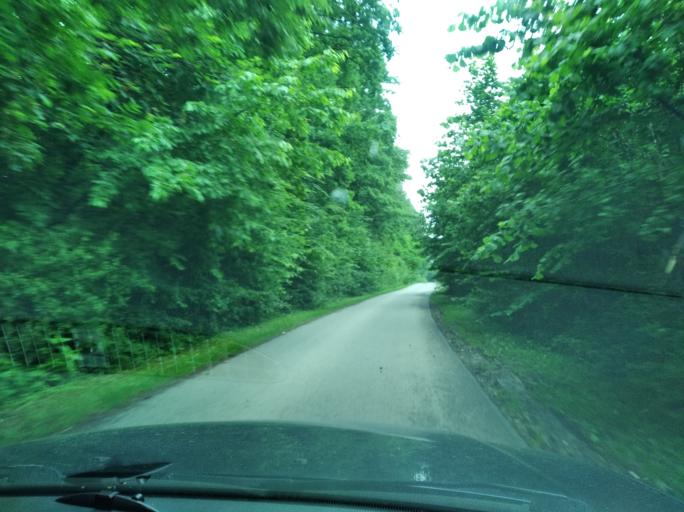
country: PL
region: Subcarpathian Voivodeship
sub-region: Powiat jaroslawski
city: Pruchnik
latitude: 49.8906
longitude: 22.5248
